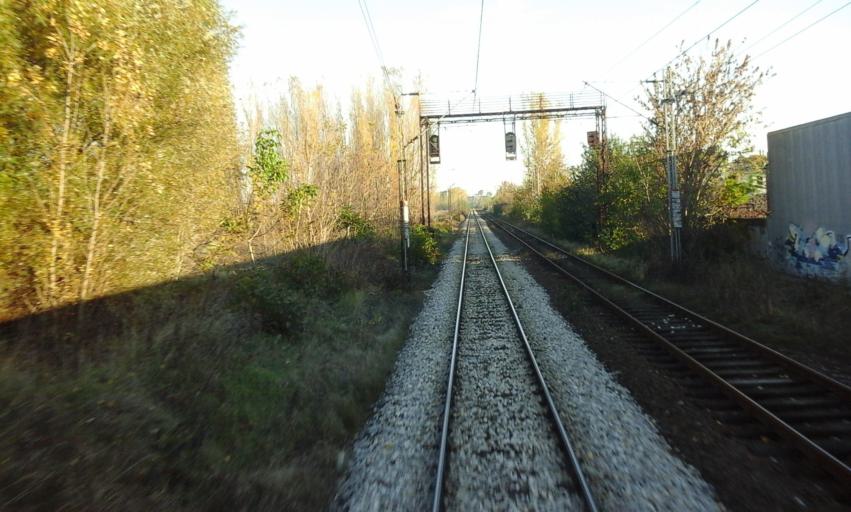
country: RS
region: Autonomna Pokrajina Vojvodina
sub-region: Juznobacki Okrug
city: Novi Sad
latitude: 45.2722
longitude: 19.8078
